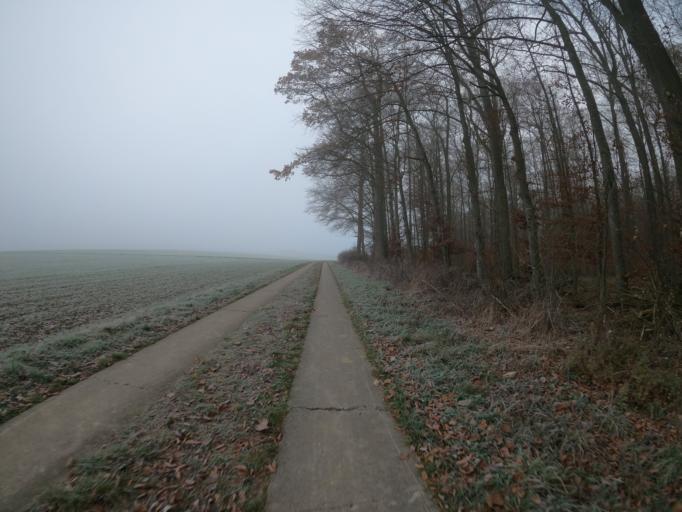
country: DE
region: Baden-Wuerttemberg
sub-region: Tuebingen Region
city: Beimerstetten
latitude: 48.4888
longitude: 9.9701
